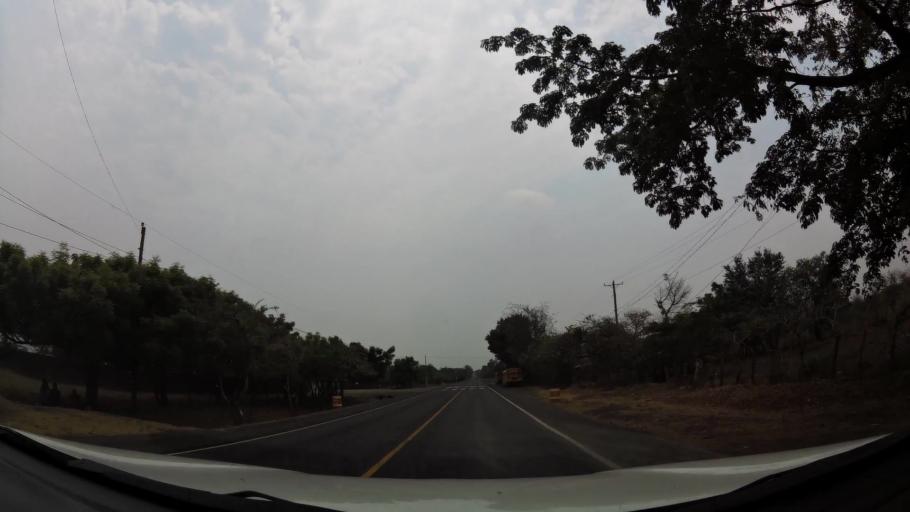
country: NI
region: Chinandega
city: Chichigalpa
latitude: 12.6054
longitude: -87.0581
